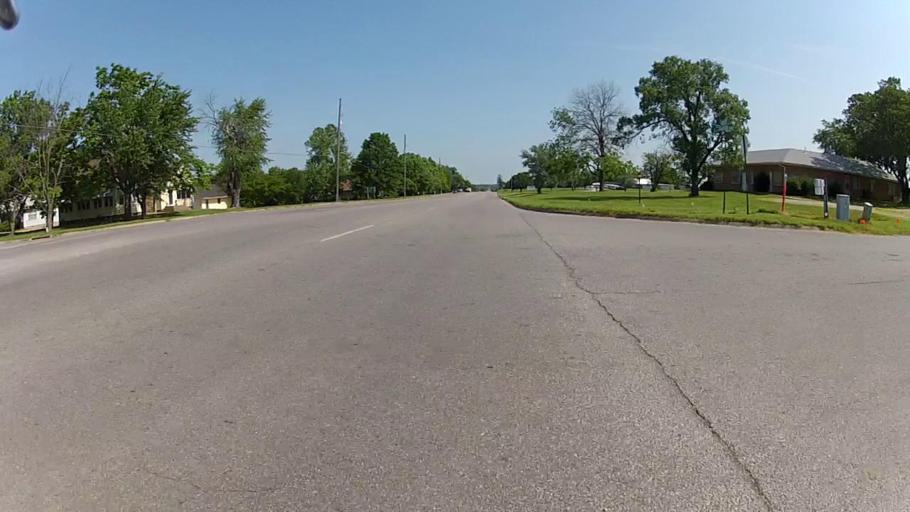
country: US
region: Kansas
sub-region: Montgomery County
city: Independence
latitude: 37.1963
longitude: -95.7106
